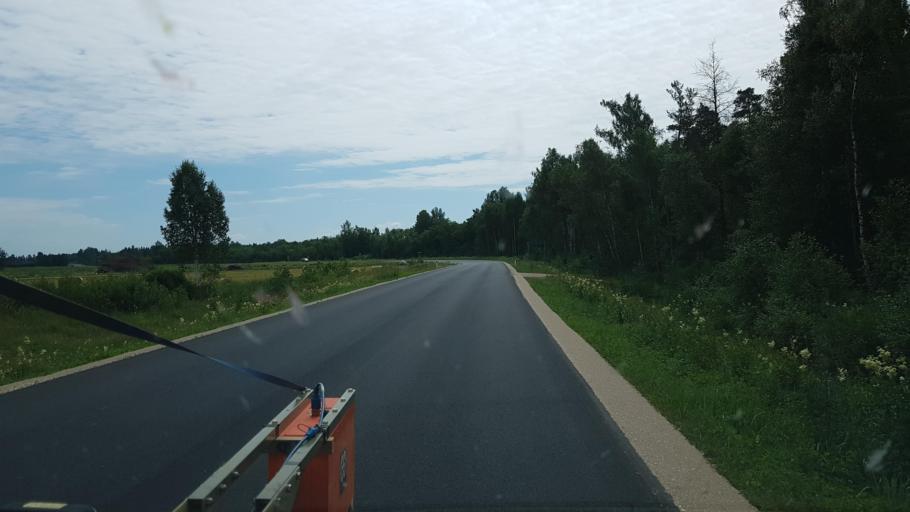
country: EE
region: Paernumaa
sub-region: Halinga vald
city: Parnu-Jaagupi
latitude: 58.6210
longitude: 24.2720
